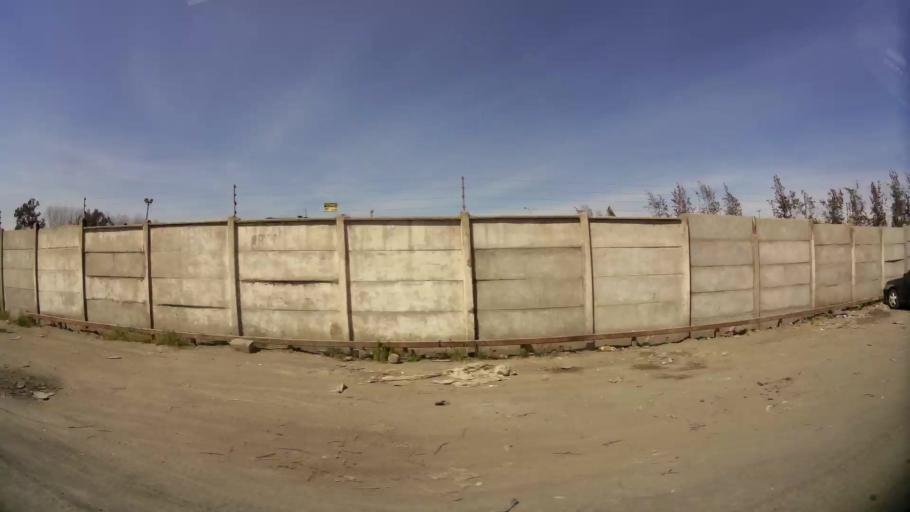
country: CL
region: Santiago Metropolitan
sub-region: Provincia de Maipo
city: San Bernardo
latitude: -33.5483
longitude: -70.6995
